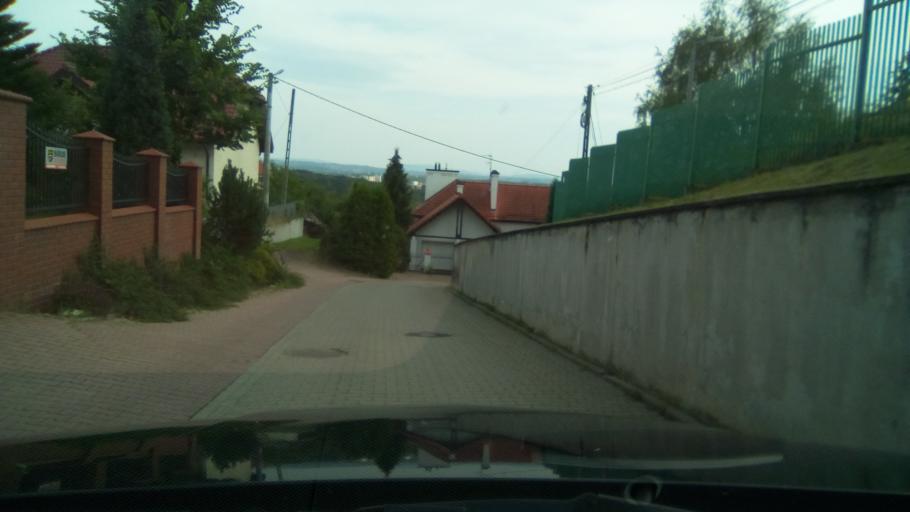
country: PL
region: Lesser Poland Voivodeship
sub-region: Krakow
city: Krakow
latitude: 50.0514
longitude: 19.8951
